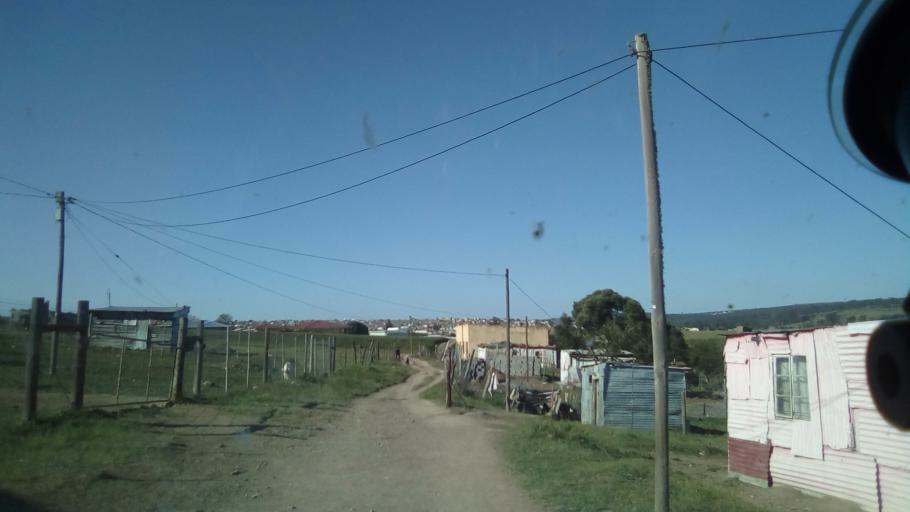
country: ZA
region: Eastern Cape
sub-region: Buffalo City Metropolitan Municipality
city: Bhisho
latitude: -32.8286
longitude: 27.3737
